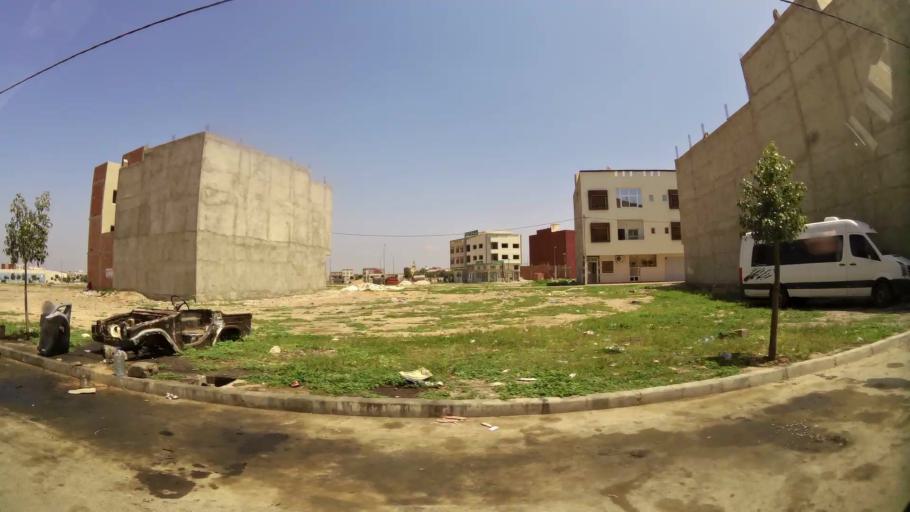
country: MA
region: Oriental
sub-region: Oujda-Angad
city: Oujda
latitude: 34.6957
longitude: -1.8944
